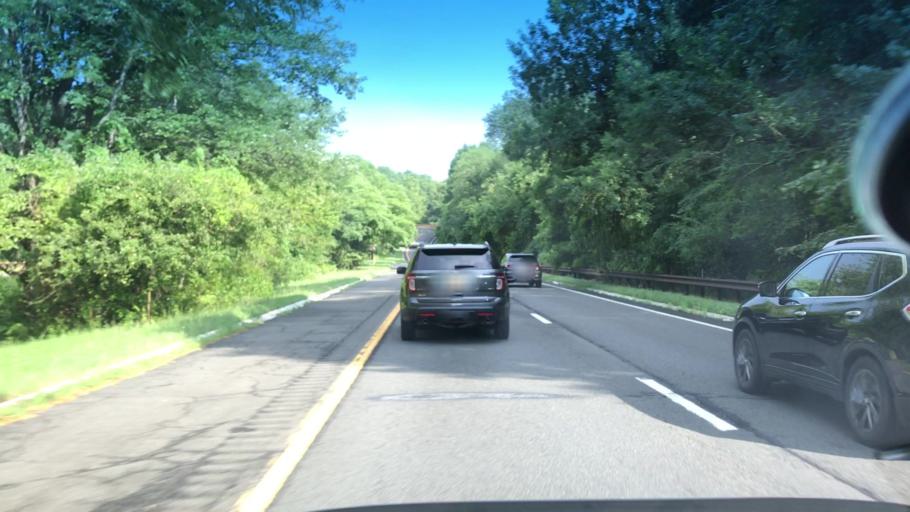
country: US
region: New York
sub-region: Rockland County
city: Sparkill
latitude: 41.0196
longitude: -73.9315
